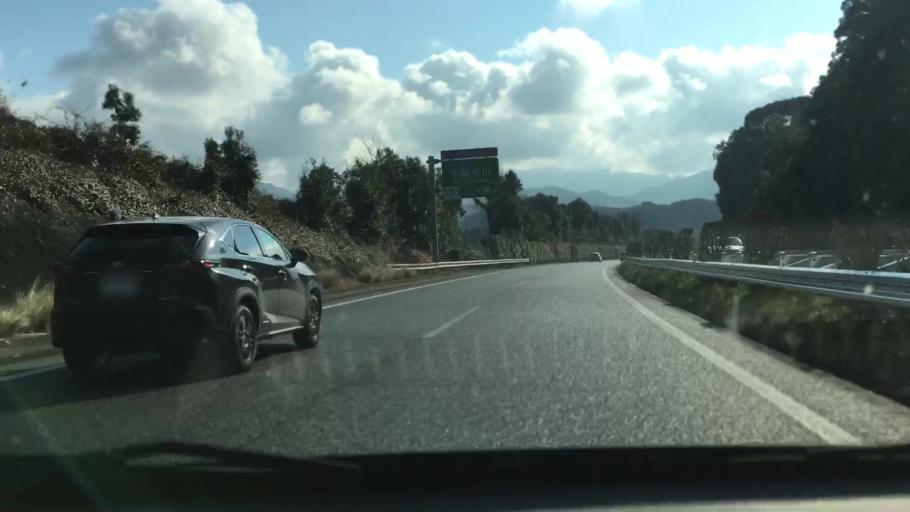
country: JP
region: Kumamoto
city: Matsubase
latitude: 32.5859
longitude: 130.7167
